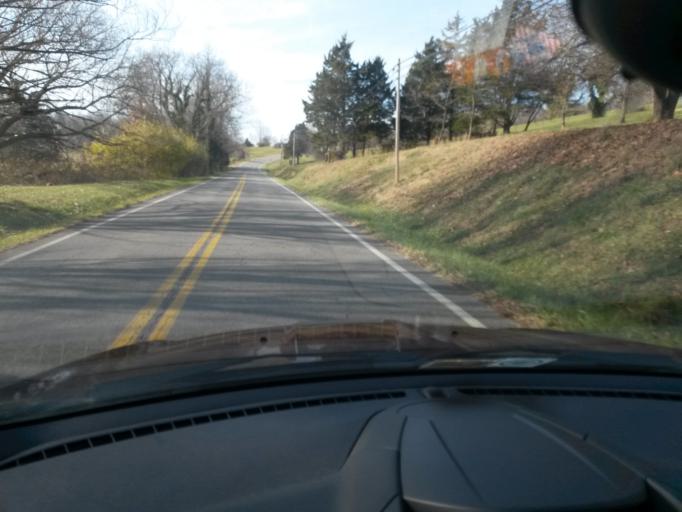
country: US
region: Virginia
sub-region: Botetourt County
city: Fincastle
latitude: 37.4975
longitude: -79.8851
